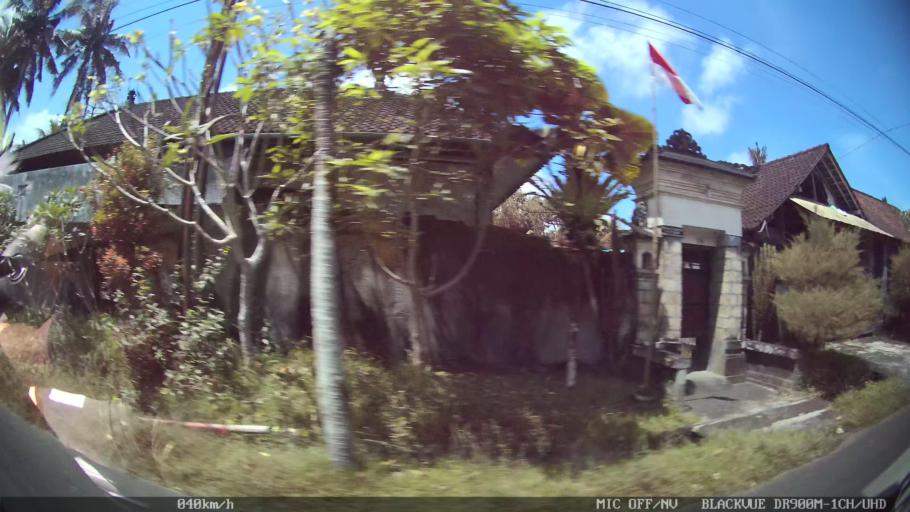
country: ID
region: Bali
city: Banjar Kelodan
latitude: -8.5222
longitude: 115.3336
